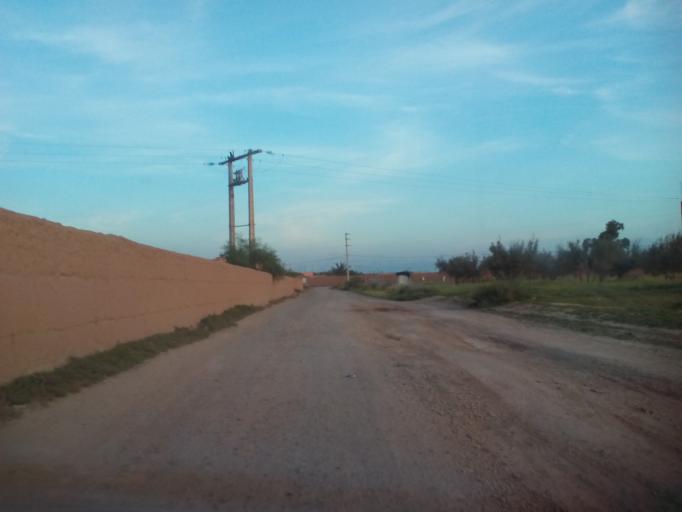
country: MA
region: Marrakech-Tensift-Al Haouz
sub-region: Marrakech
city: Marrakesh
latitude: 31.6259
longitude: -8.2847
